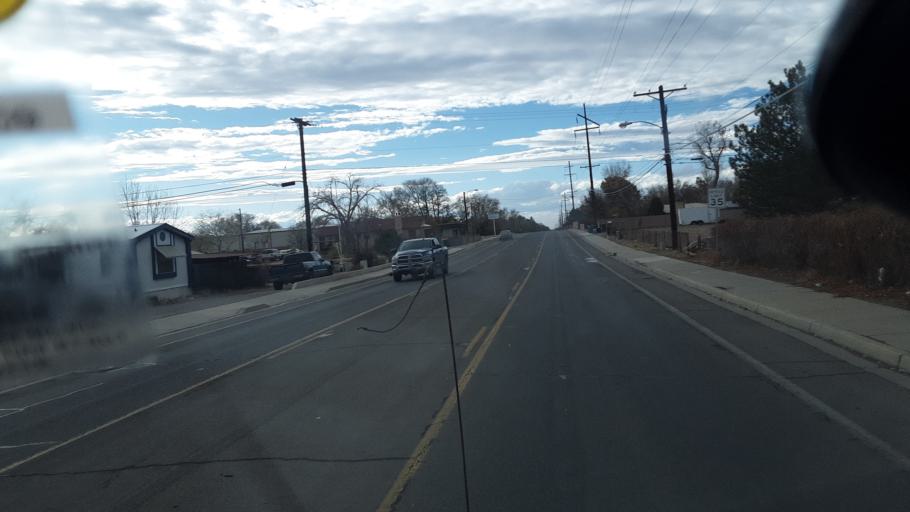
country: US
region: New Mexico
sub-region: San Juan County
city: Farmington
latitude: 36.7265
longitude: -108.1704
